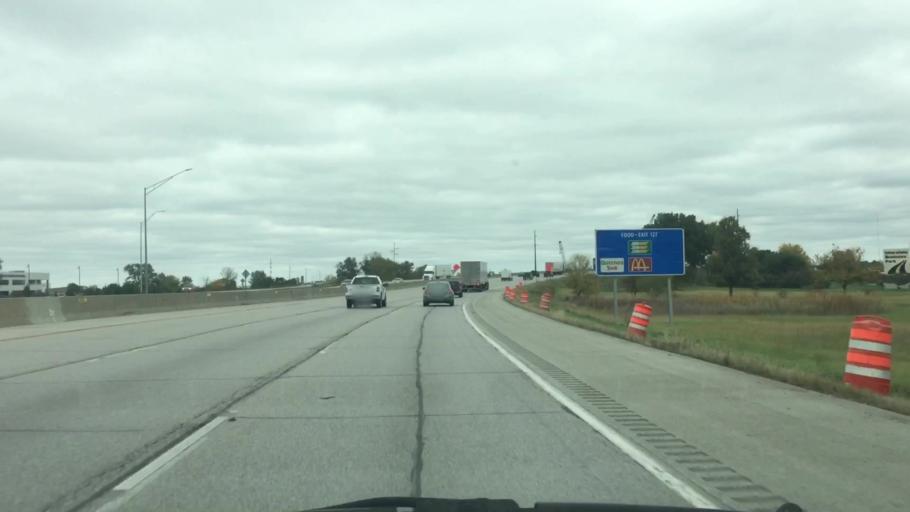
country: US
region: Iowa
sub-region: Polk County
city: Grimes
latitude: 41.6448
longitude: -93.7767
